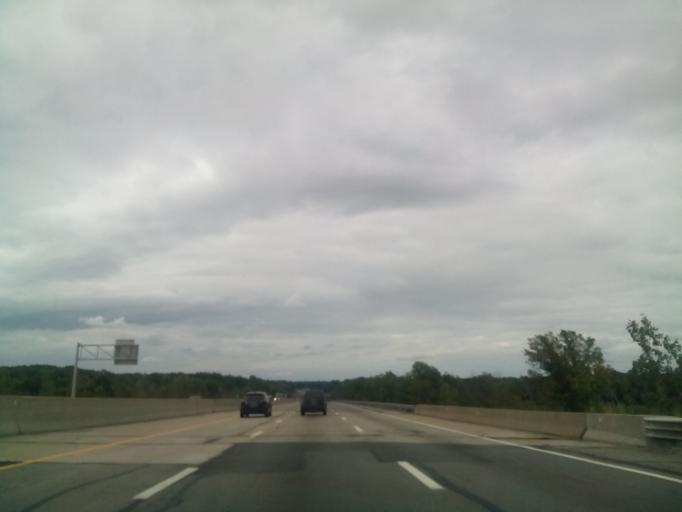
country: US
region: Ohio
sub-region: Lorain County
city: South Amherst
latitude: 41.3769
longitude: -82.2488
